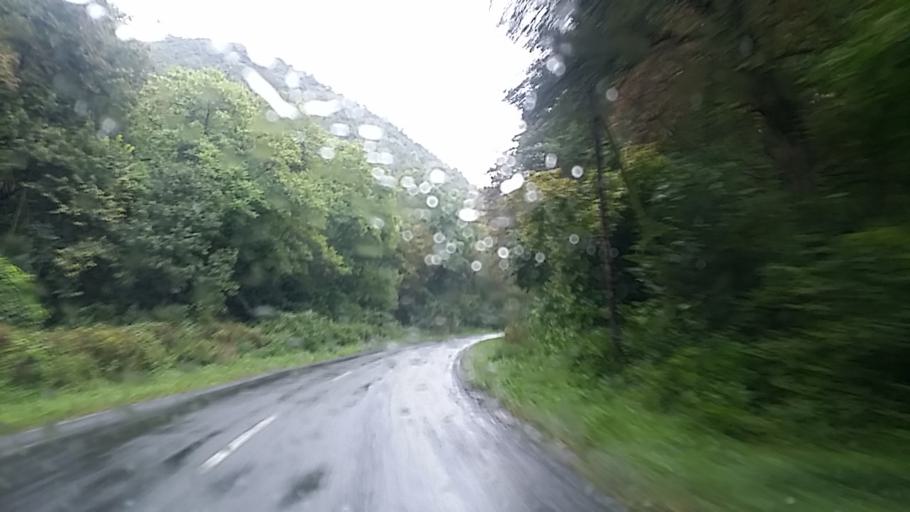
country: HU
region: Komarom-Esztergom
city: Kesztolc
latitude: 47.7440
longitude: 18.8061
